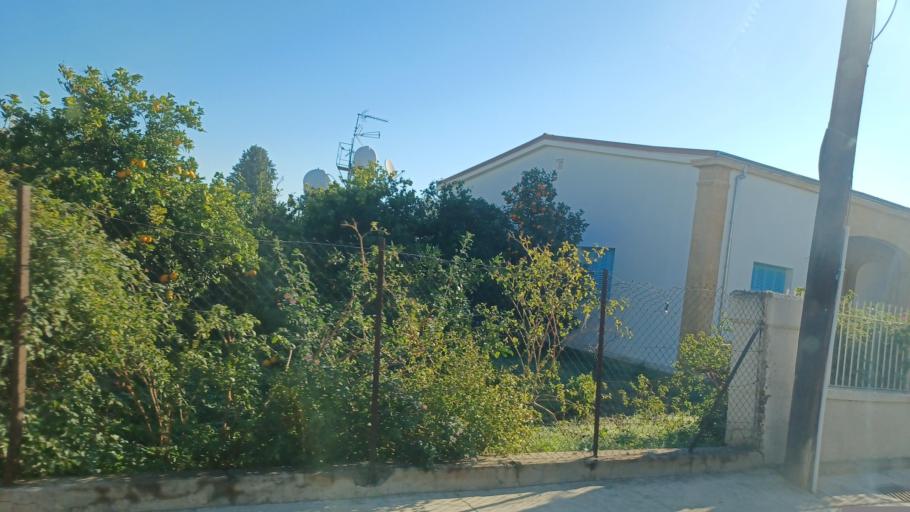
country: CY
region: Lefkosia
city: Nicosia
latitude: 35.1488
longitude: 33.3402
